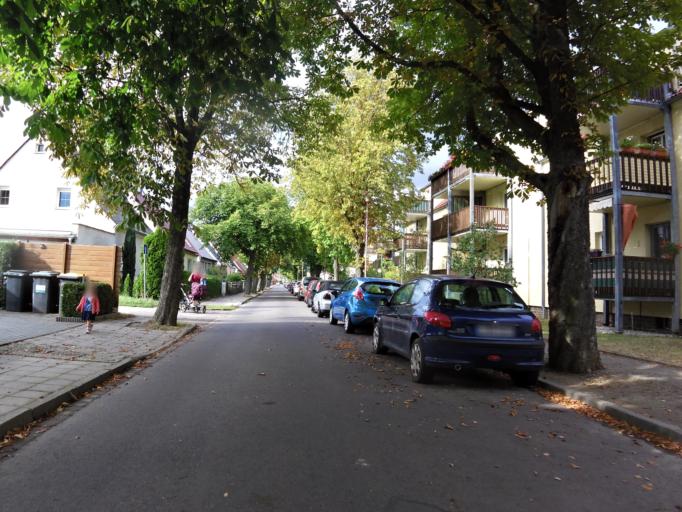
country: DE
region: Saxony
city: Schkeuditz
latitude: 51.3531
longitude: 12.2849
